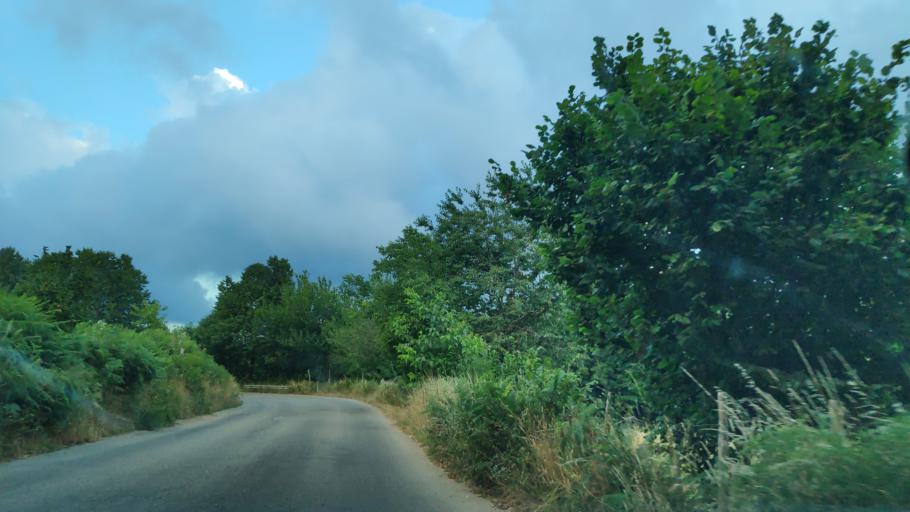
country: IT
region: Calabria
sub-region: Provincia di Vibo-Valentia
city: Mongiana
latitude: 38.5363
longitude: 16.3184
